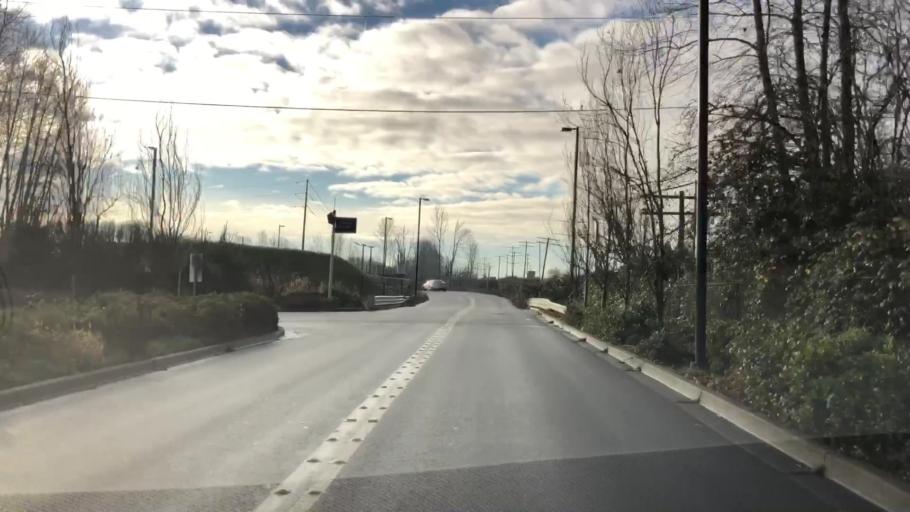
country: US
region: Washington
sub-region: King County
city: Tukwila
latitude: 47.4590
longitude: -122.2419
